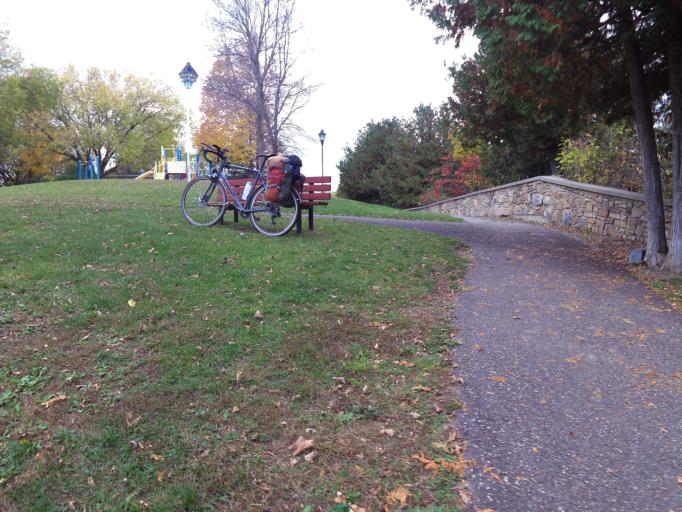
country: CA
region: Ontario
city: Pembroke
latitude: 45.5387
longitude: -77.0978
